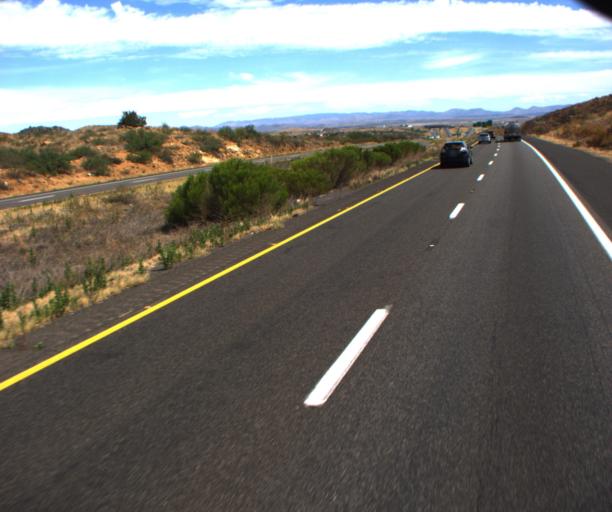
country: US
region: Arizona
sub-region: Yavapai County
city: Cordes Lakes
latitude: 34.3100
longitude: -112.1258
